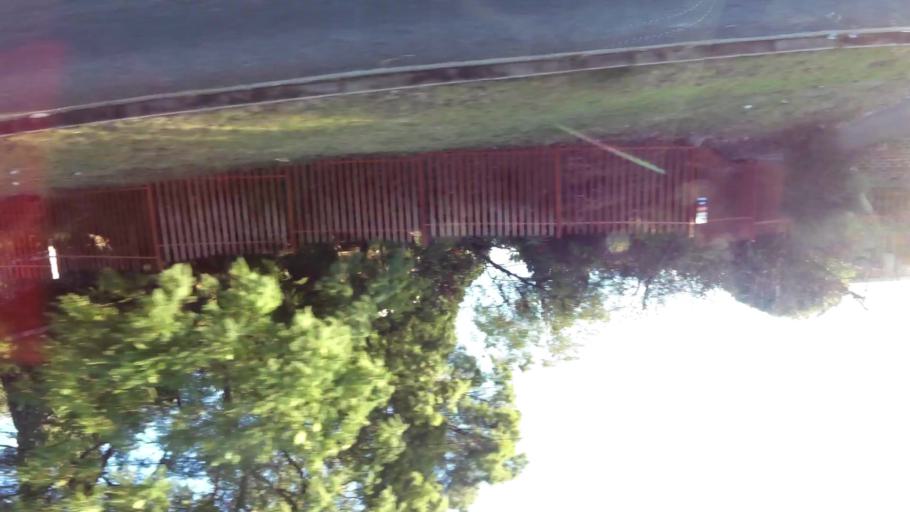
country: ZA
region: Gauteng
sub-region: City of Johannesburg Metropolitan Municipality
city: Roodepoort
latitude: -26.1667
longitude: 27.9450
